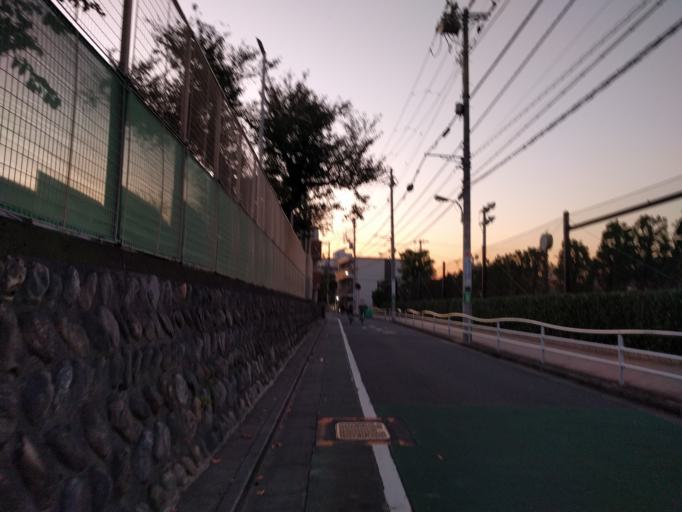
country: JP
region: Tokyo
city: Tokyo
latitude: 35.6444
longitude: 139.6304
